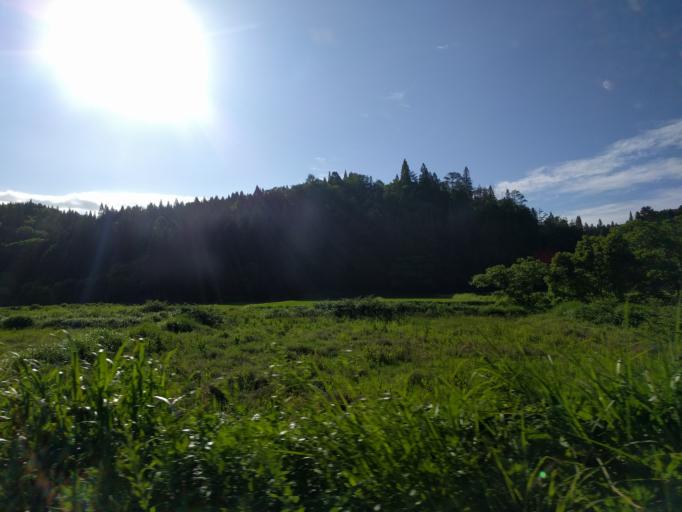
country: JP
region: Fukushima
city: Kitakata
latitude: 37.4239
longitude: 139.8105
